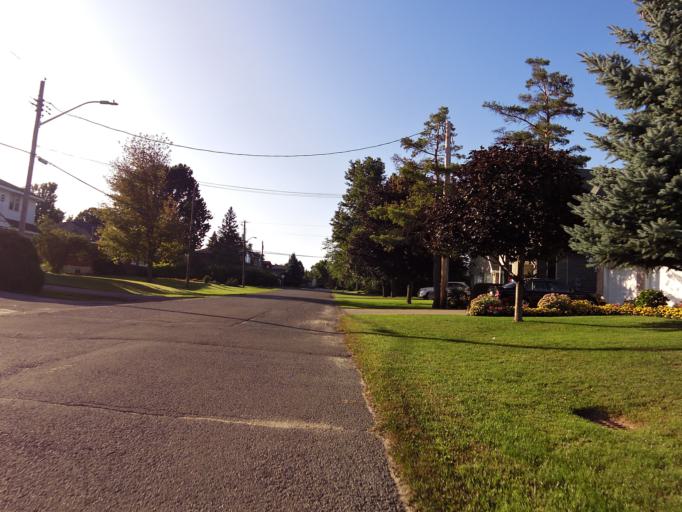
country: CA
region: Ontario
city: Ottawa
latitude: 45.3564
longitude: -75.7121
